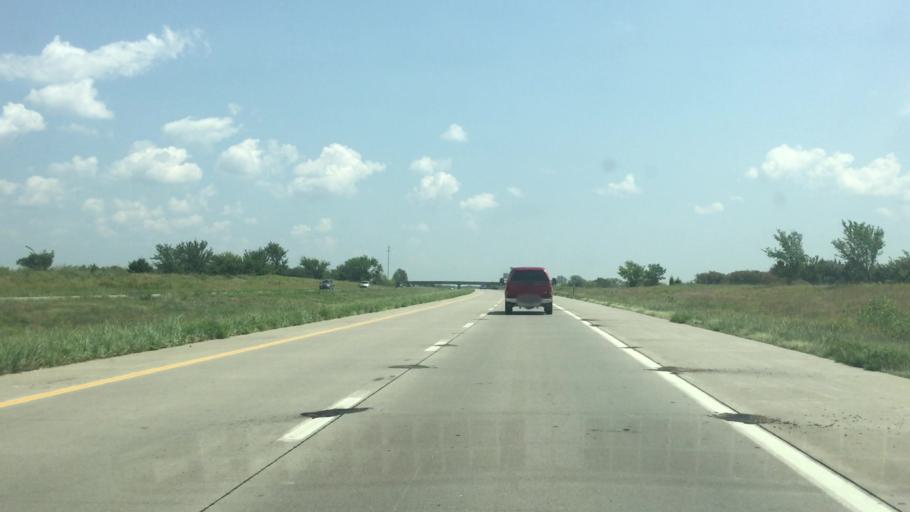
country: US
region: Kansas
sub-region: Franklin County
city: Wellsville
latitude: 38.6811
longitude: -95.1275
